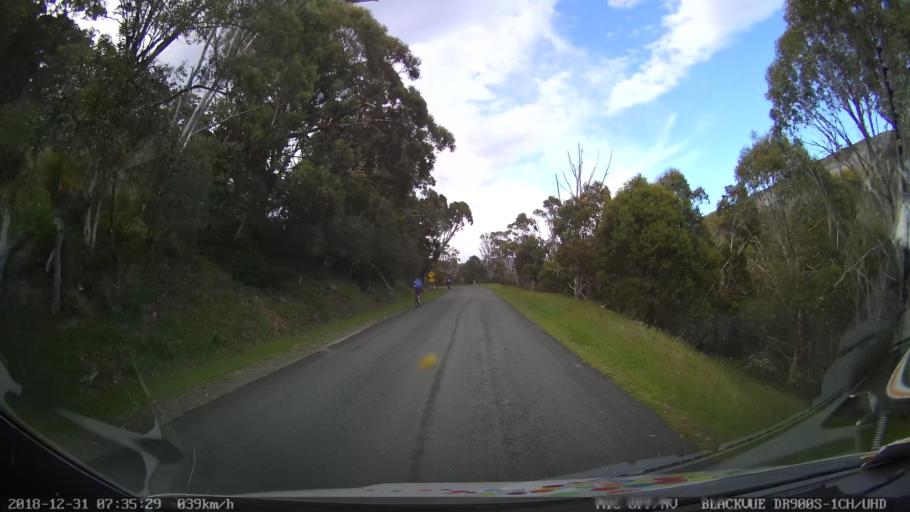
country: AU
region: New South Wales
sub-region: Snowy River
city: Jindabyne
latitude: -36.3353
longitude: 148.4447
